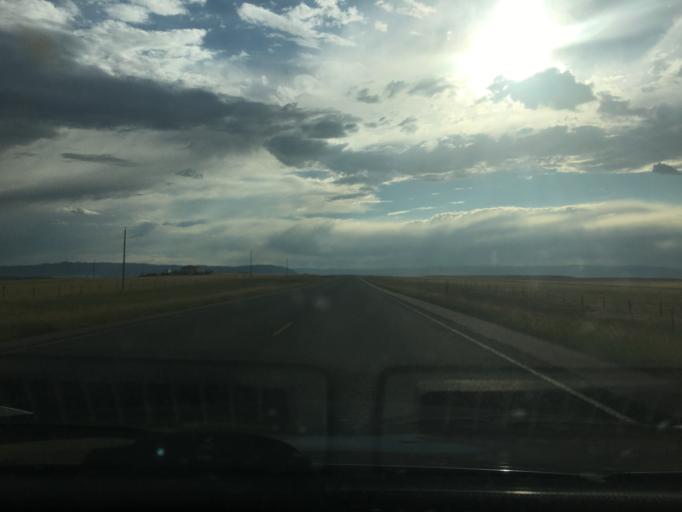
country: US
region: Wyoming
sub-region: Albany County
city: Laramie
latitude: 41.3262
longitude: -105.7283
